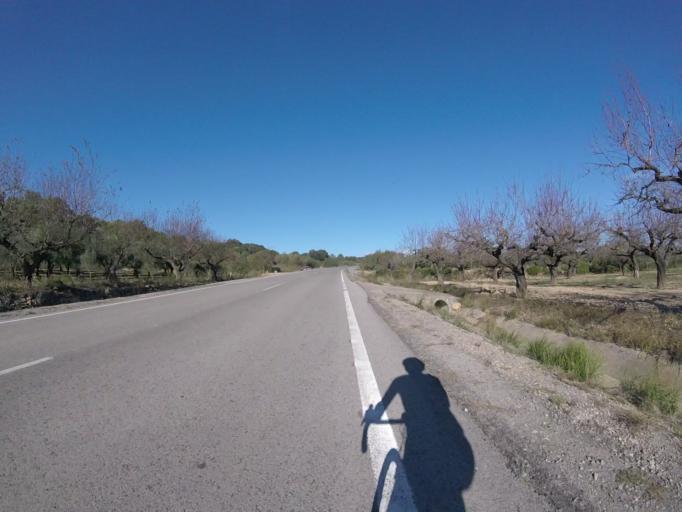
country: ES
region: Valencia
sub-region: Provincia de Castello
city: Cervera del Maestre
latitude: 40.4701
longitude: 0.2434
